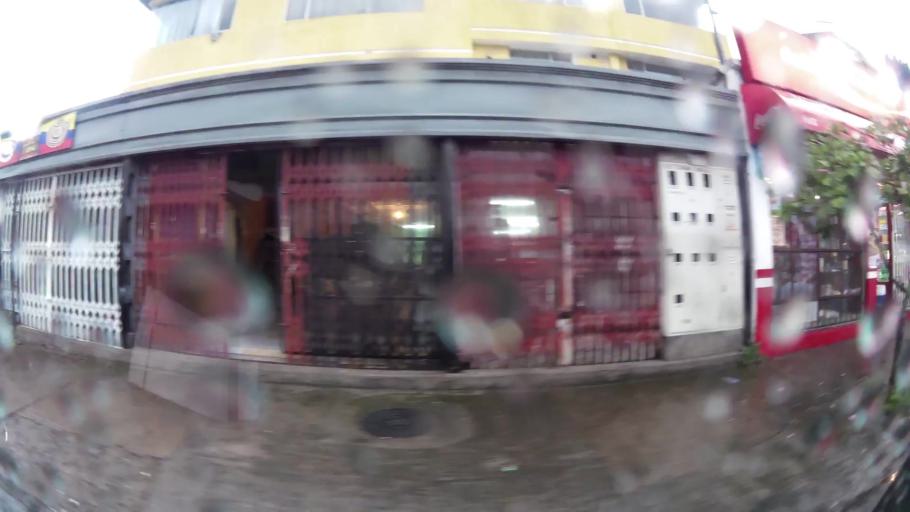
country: EC
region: Pichincha
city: Quito
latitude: -0.1587
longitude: -78.4642
